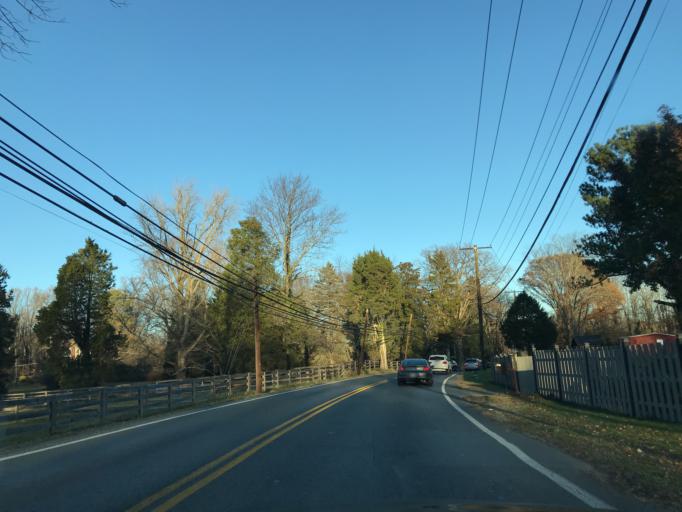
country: US
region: Maryland
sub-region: Montgomery County
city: Olney
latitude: 39.1463
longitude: -77.0402
